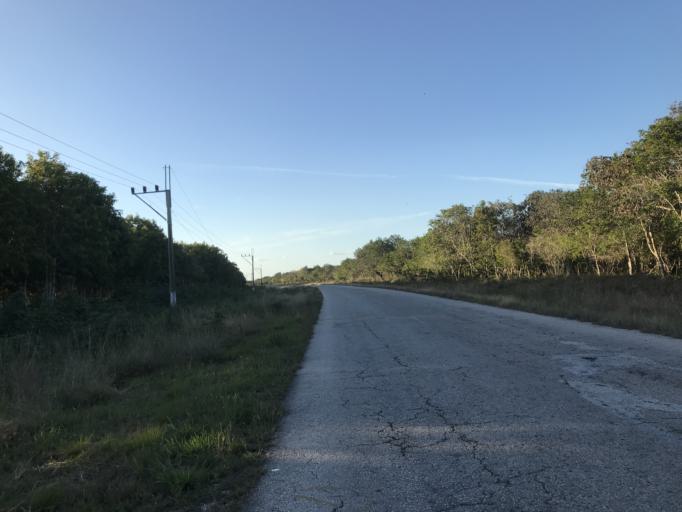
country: CU
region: Cienfuegos
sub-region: Municipio de Aguada de Pasajeros
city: Aguada de Pasajeros
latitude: 22.0723
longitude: -81.0559
